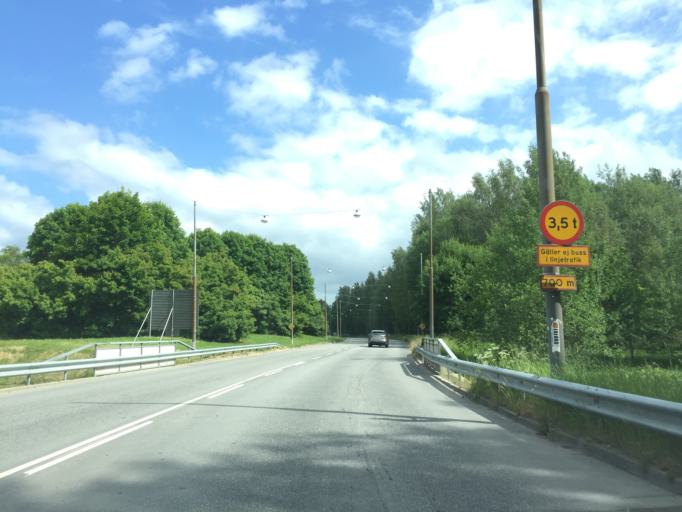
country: SE
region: OErebro
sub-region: Orebro Kommun
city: Orebro
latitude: 59.2412
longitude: 15.1562
